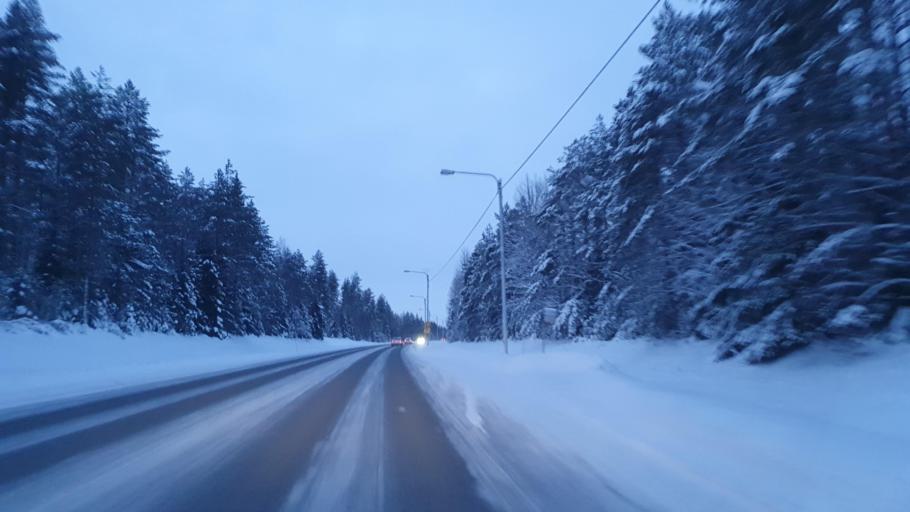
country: FI
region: Northern Ostrobothnia
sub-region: Oulu
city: Tyrnaevae
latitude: 64.9345
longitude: 25.7150
